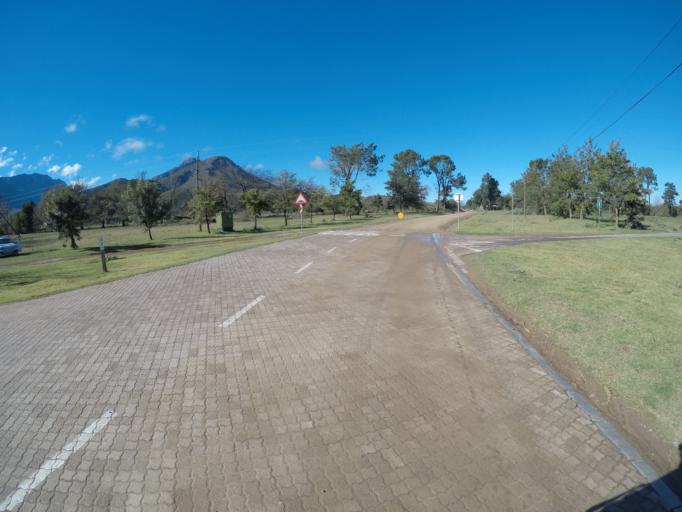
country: ZA
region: Western Cape
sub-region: Overberg District Municipality
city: Caledon
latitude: -34.0511
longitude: 19.6107
